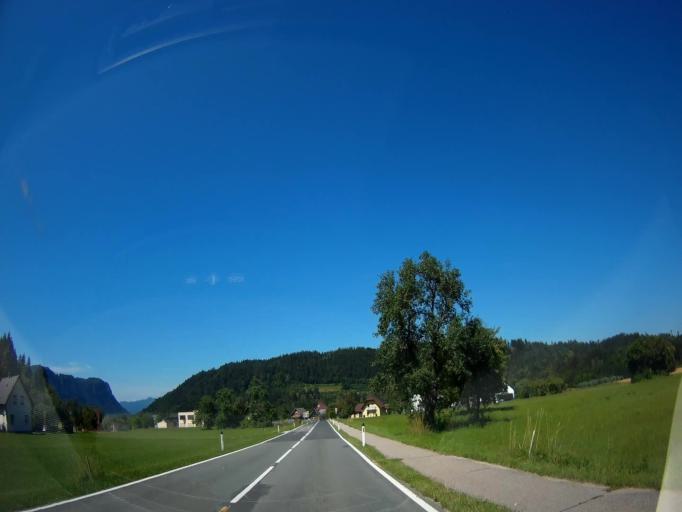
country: AT
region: Carinthia
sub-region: Politischer Bezirk Volkermarkt
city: Gallizien
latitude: 46.5490
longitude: 14.5131
